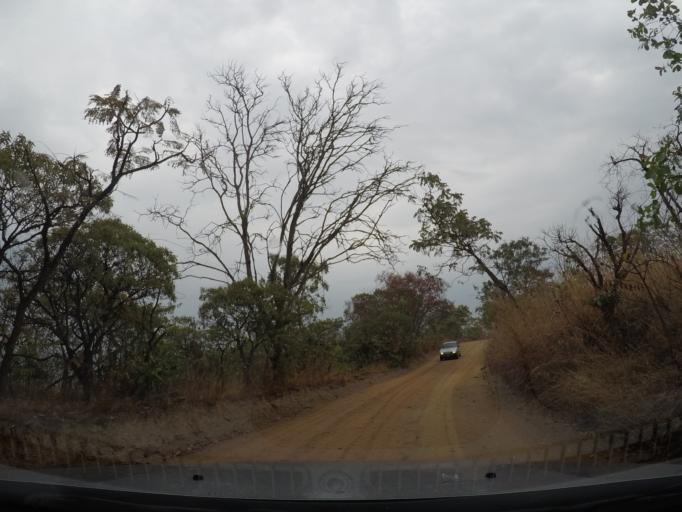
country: BR
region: Goias
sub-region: Pirenopolis
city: Pirenopolis
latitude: -15.8310
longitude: -48.9087
